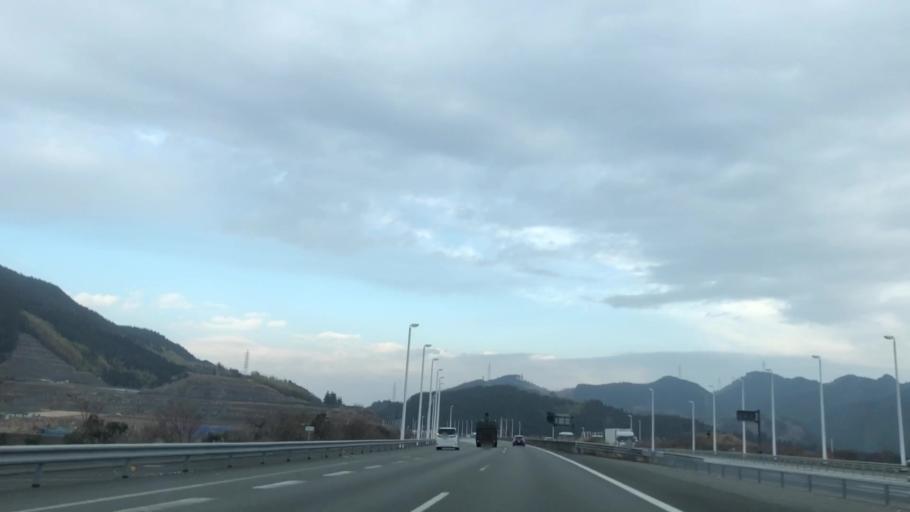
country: JP
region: Shizuoka
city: Fujinomiya
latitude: 35.1296
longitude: 138.5065
